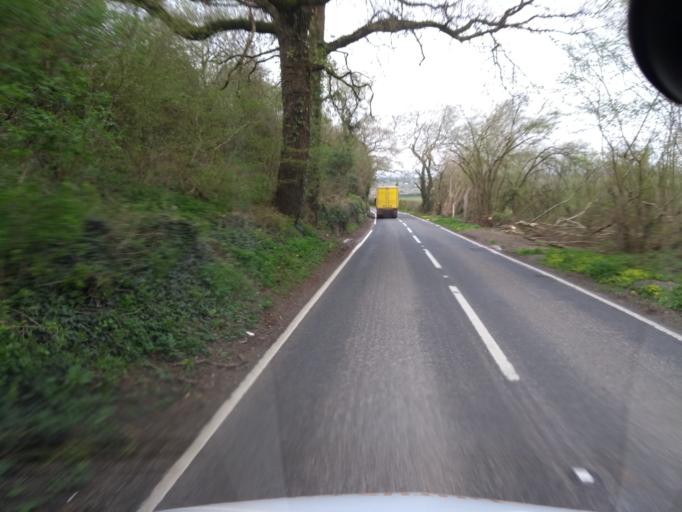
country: GB
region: England
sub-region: Somerset
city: Curry Rivel
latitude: 51.0042
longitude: -2.9475
